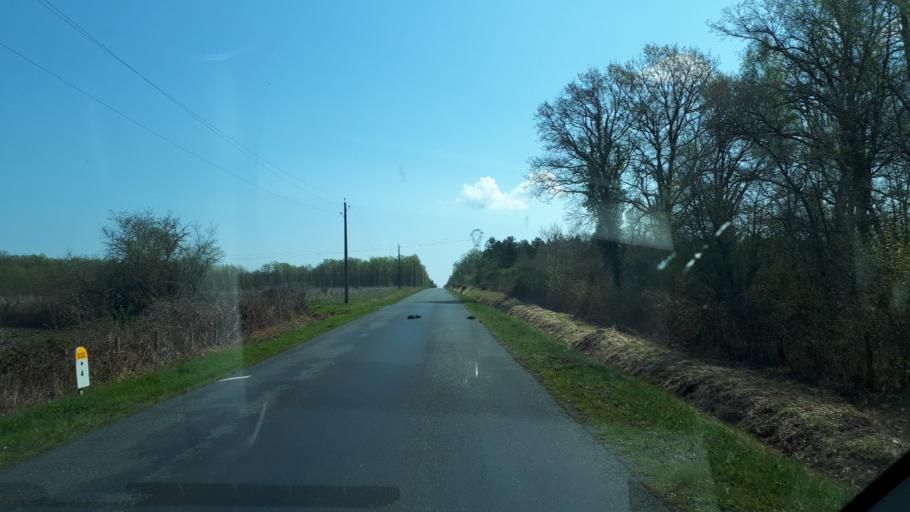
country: FR
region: Centre
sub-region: Departement du Cher
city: Neuvy-sur-Barangeon
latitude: 47.3202
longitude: 2.1927
